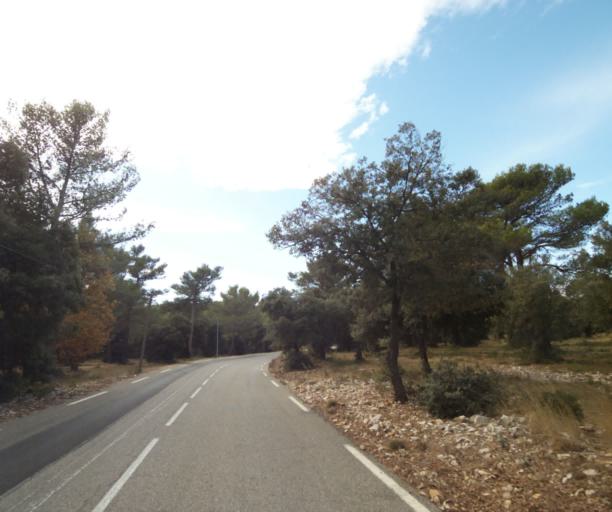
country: FR
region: Provence-Alpes-Cote d'Azur
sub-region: Departement des Bouches-du-Rhone
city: Cuges-les-Pins
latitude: 43.2389
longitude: 5.6872
